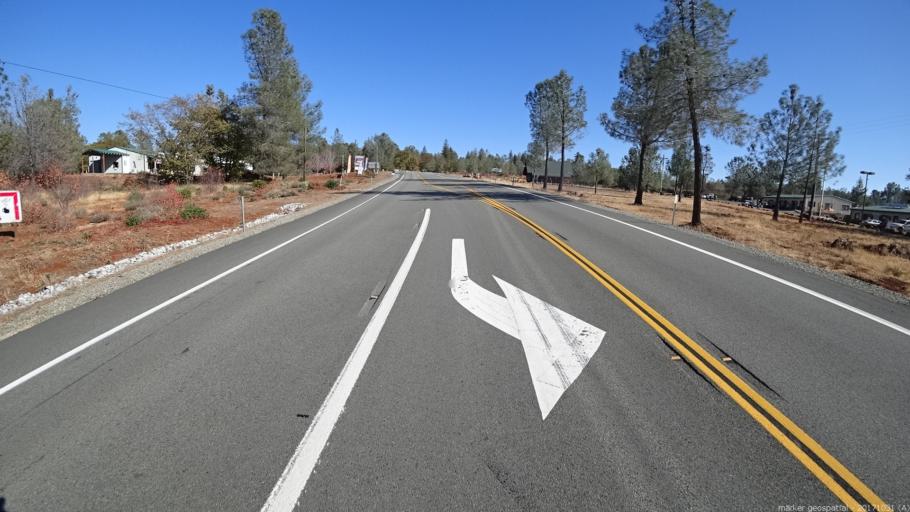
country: US
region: California
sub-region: Shasta County
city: Shingletown
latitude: 40.5016
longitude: -121.9939
